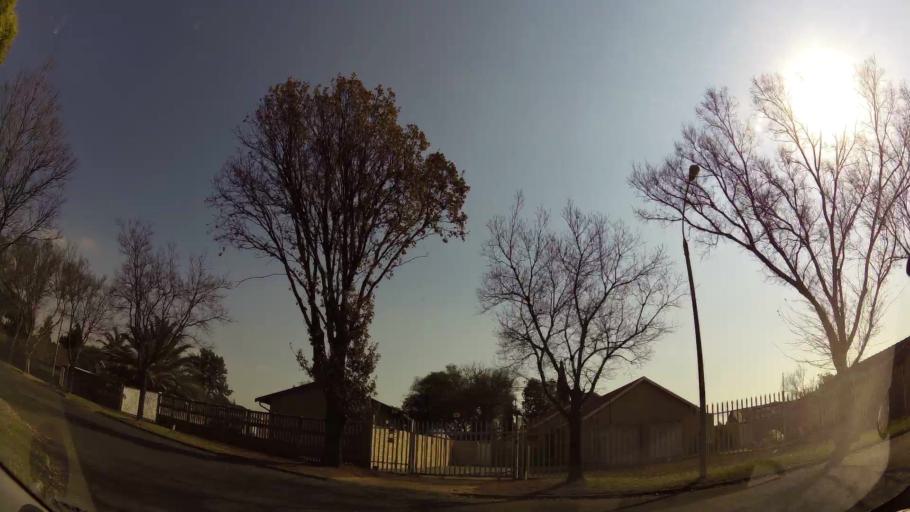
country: ZA
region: Gauteng
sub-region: Ekurhuleni Metropolitan Municipality
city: Benoni
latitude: -26.1506
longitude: 28.2811
